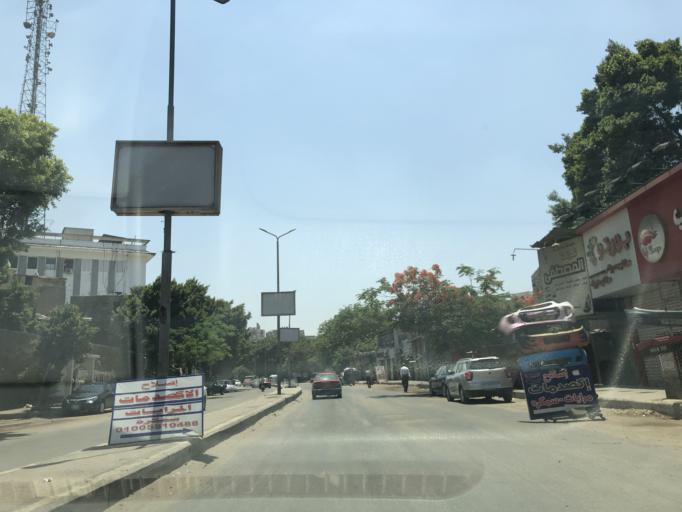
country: EG
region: Muhafazat al Qahirah
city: Cairo
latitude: 30.0675
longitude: 31.2707
